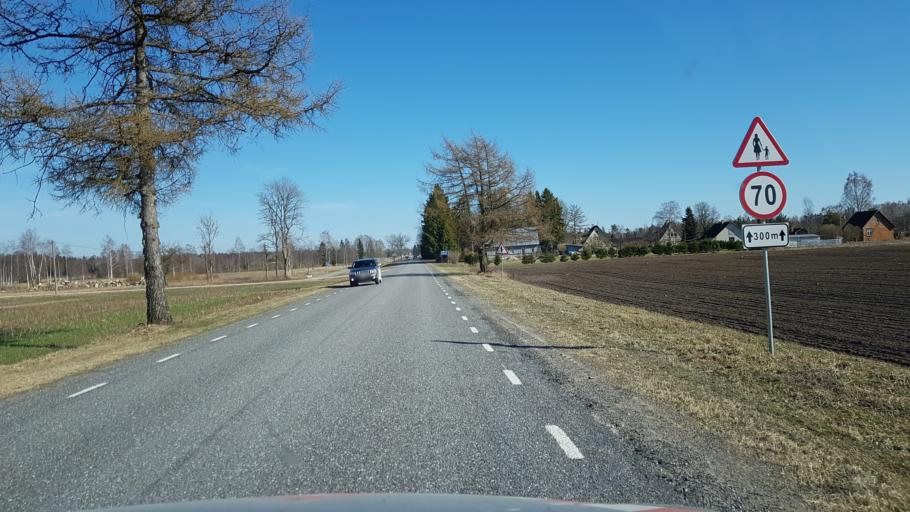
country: EE
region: Laeaene-Virumaa
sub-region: Rakke vald
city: Rakke
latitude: 59.0002
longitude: 26.2001
